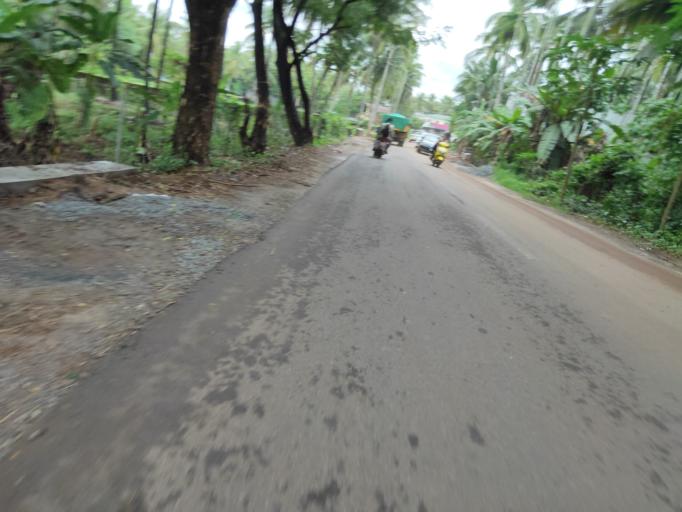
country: IN
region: Kerala
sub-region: Malappuram
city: Manjeri
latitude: 11.1980
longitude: 76.2203
